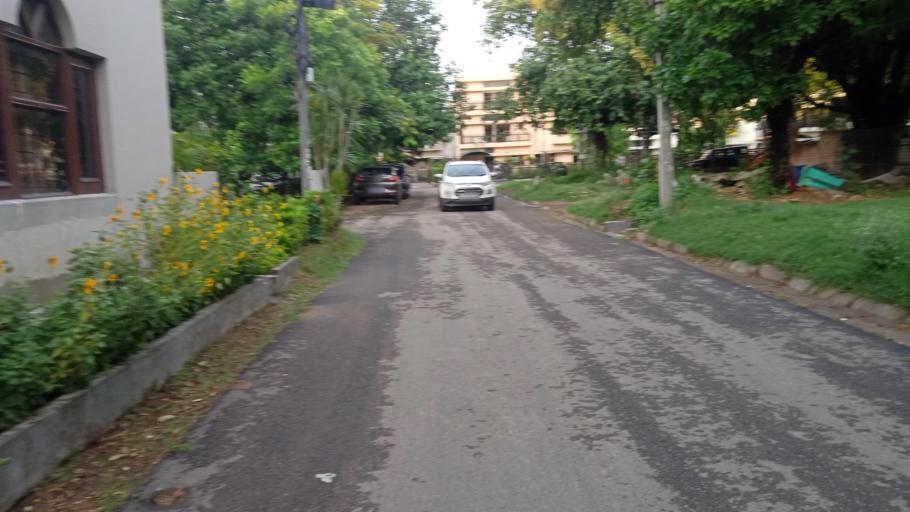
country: IN
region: Chandigarh
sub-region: Chandigarh
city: Chandigarh
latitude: 30.7469
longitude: 76.7482
